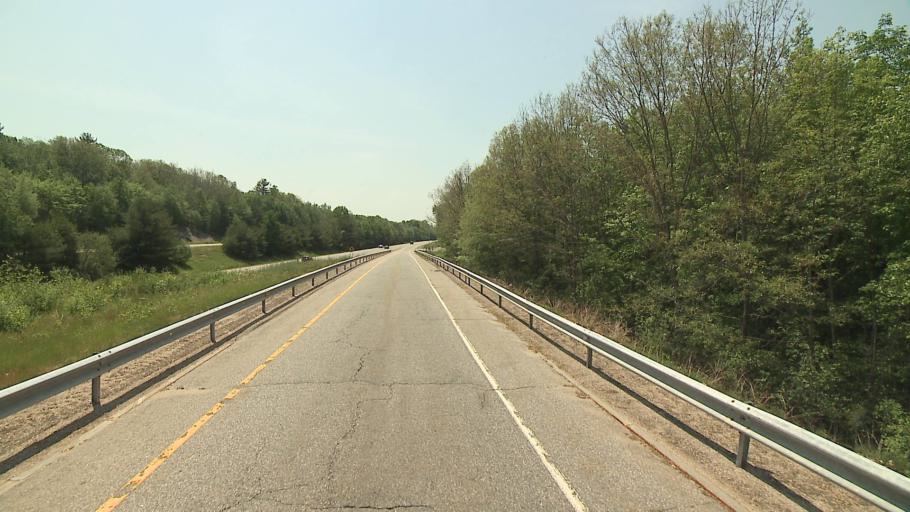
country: US
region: Connecticut
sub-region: Windham County
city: Thompson
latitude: 41.9657
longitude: -71.8735
